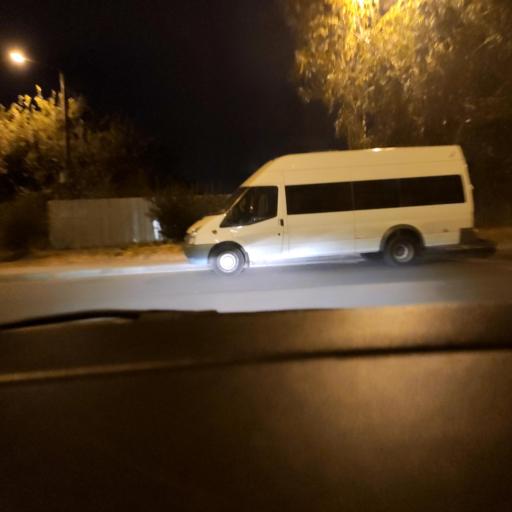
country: RU
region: Voronezj
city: Voronezh
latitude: 51.6911
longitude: 39.2119
